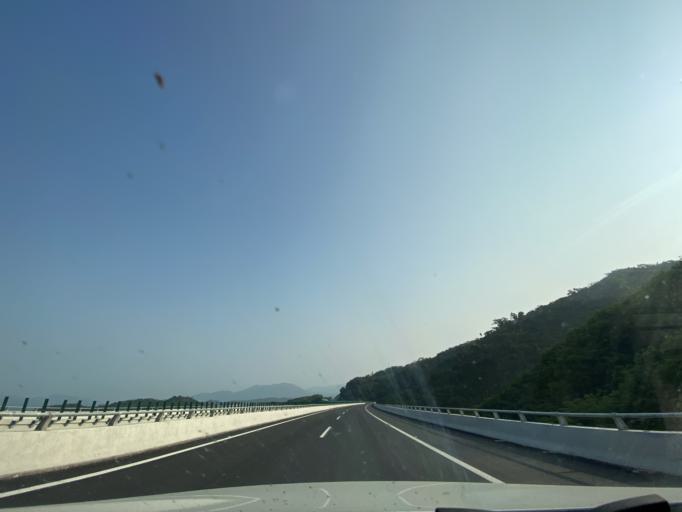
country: CN
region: Hainan
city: Xiangshui
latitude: 18.6585
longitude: 109.6290
